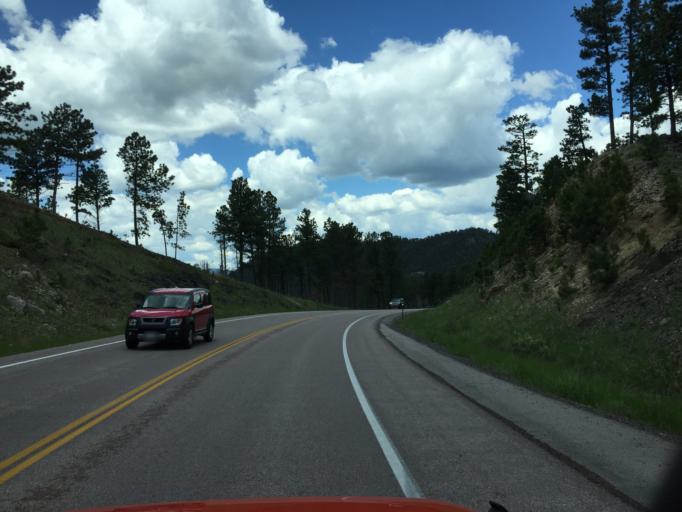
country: US
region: South Dakota
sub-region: Custer County
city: Custer
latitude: 43.8982
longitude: -103.5247
